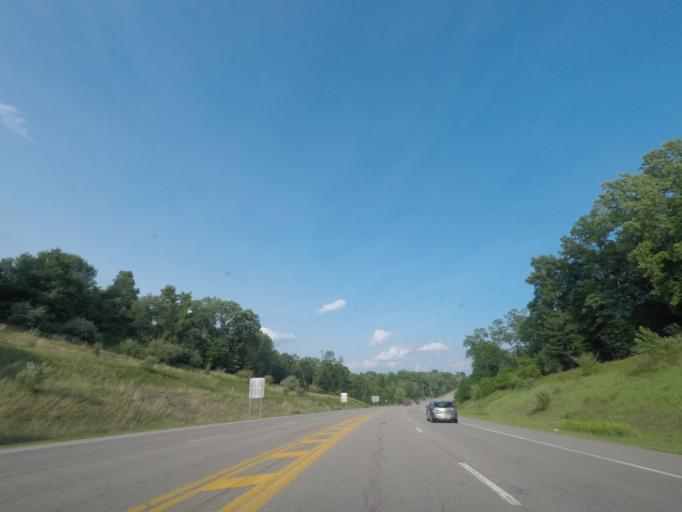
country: US
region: New York
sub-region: Orange County
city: Orange Lake
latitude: 41.4975
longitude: -74.1167
